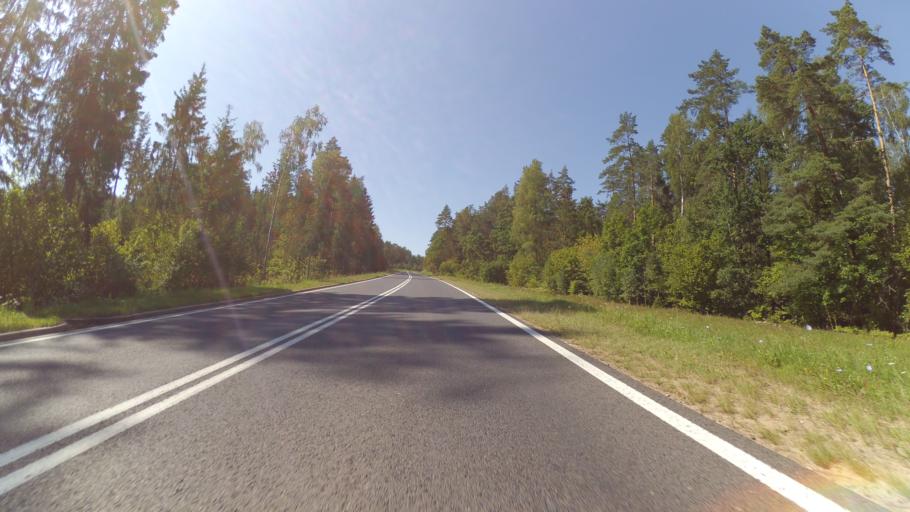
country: PL
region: Podlasie
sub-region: Powiat bialostocki
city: Michalowo
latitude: 53.1429
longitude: 23.4927
